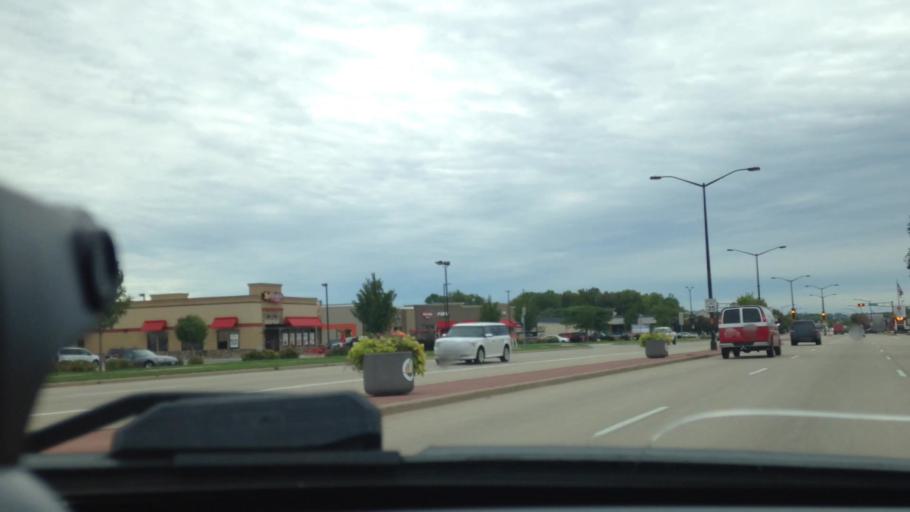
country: US
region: Wisconsin
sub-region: Fond du Lac County
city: North Fond du Lac
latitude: 43.7842
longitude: -88.4756
